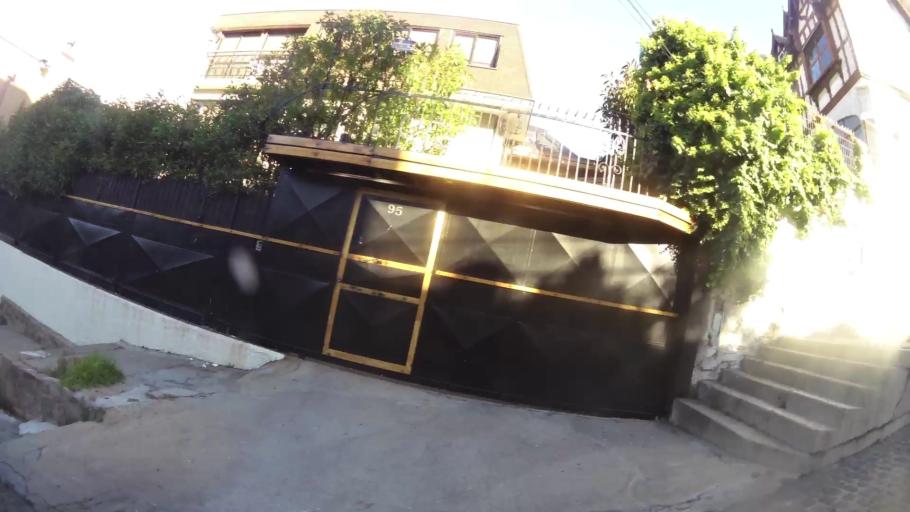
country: CL
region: Valparaiso
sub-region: Provincia de Valparaiso
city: Vina del Mar
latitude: -33.0290
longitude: -71.5778
